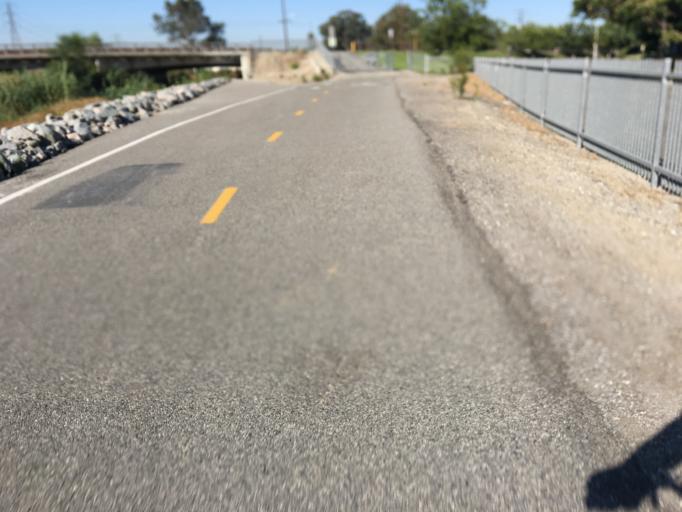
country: US
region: California
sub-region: Los Angeles County
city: West Whittier-Los Nietos
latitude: 34.0144
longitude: -118.0627
